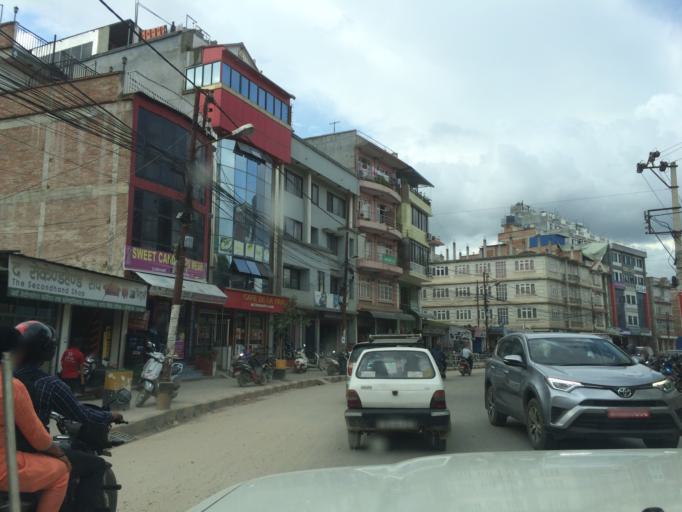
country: NP
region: Central Region
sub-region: Bagmati Zone
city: Kathmandu
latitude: 27.7161
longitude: 85.3039
